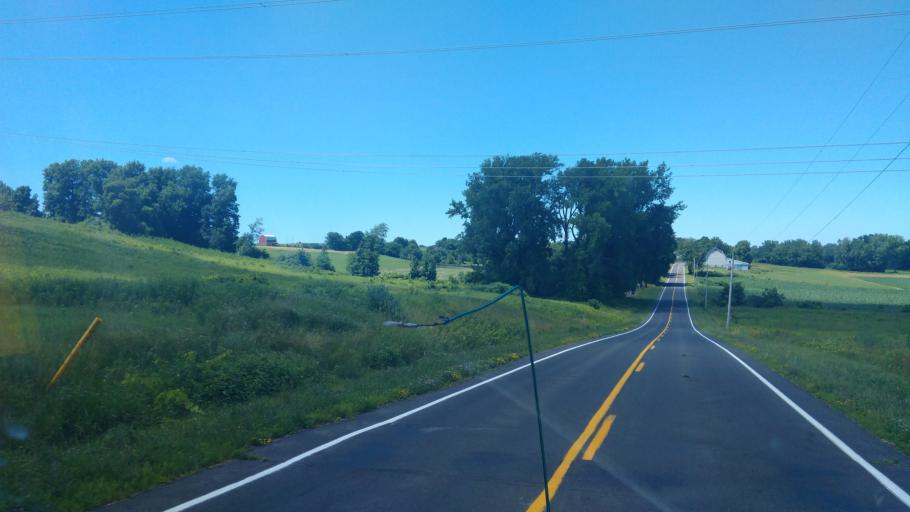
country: US
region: New York
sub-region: Wayne County
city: Lyons
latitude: 43.1299
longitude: -76.9587
